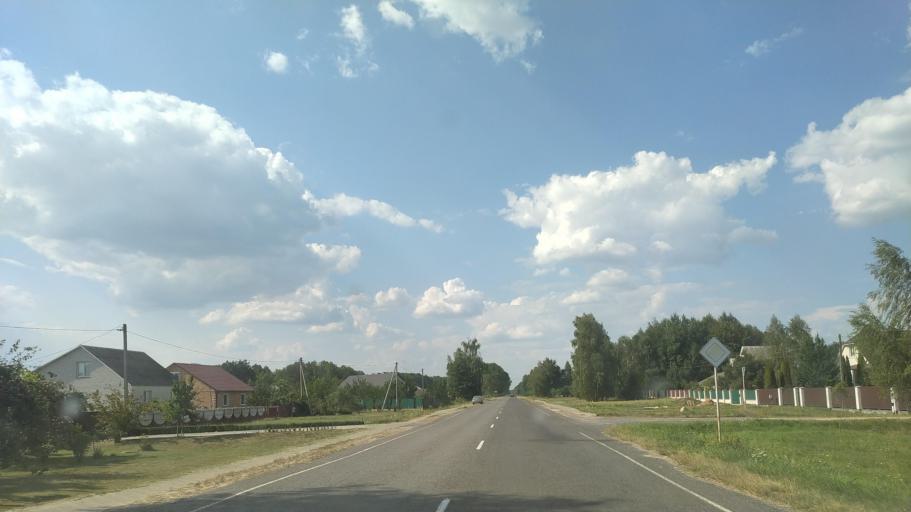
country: BY
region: Brest
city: Drahichyn
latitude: 52.2056
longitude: 25.1432
